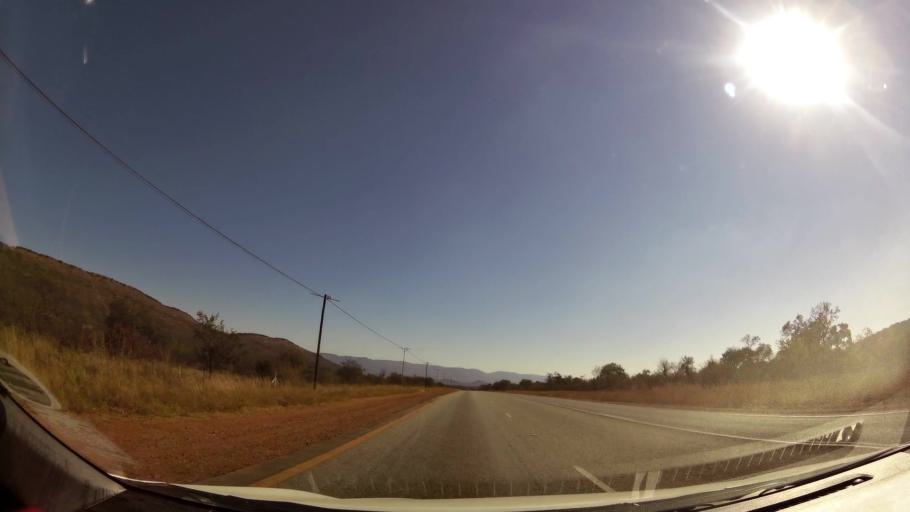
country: ZA
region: Limpopo
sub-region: Waterberg District Municipality
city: Mokopane
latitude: -24.1637
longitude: 29.0652
